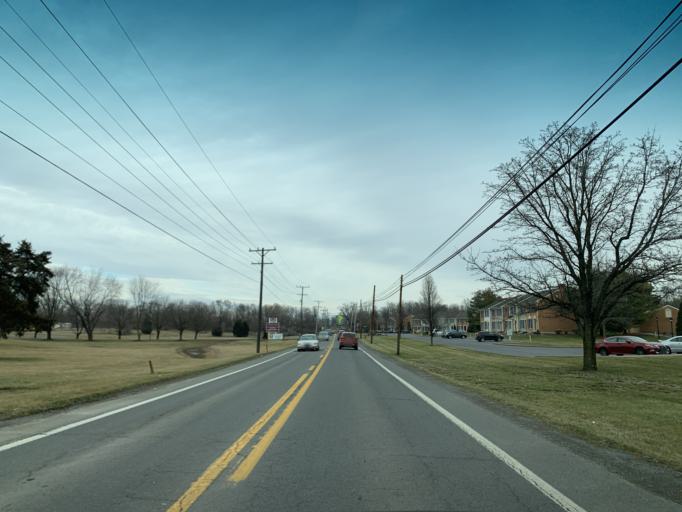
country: US
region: West Virginia
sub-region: Berkeley County
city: Martinsburg
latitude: 39.5025
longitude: -77.9381
